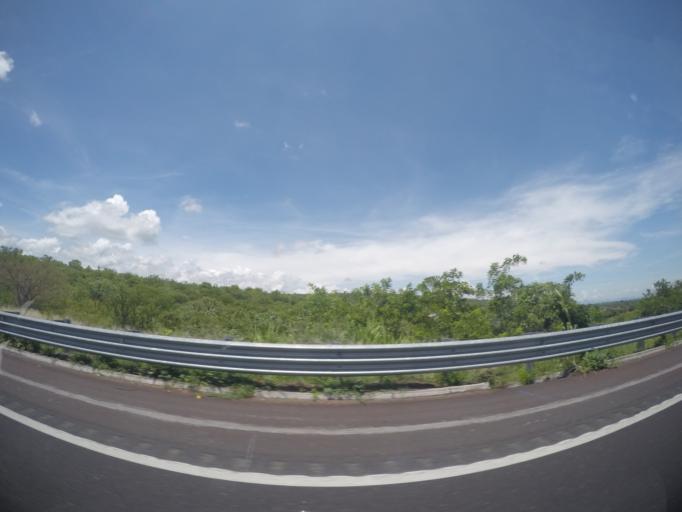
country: MX
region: Morelos
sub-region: Jojutla
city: Higueron
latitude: 18.5546
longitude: -99.2096
